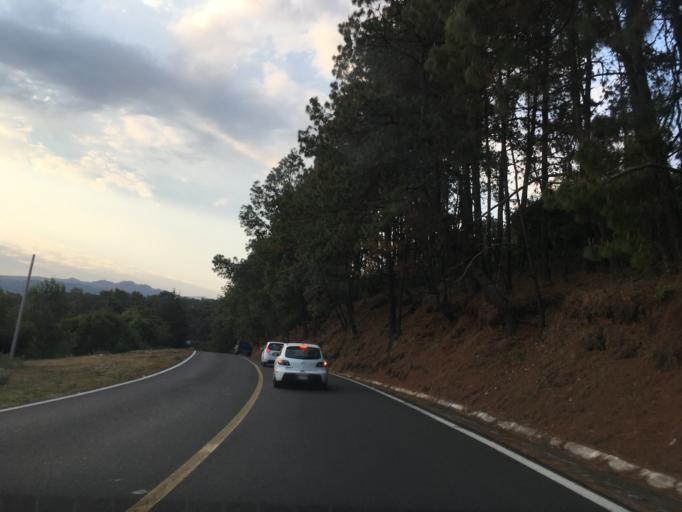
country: MX
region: Michoacan
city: Tingambato
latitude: 19.5048
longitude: -101.8350
